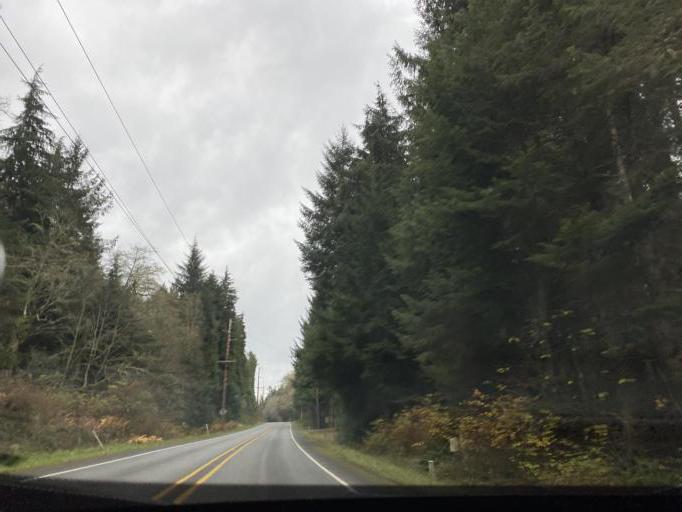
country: US
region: Washington
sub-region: Island County
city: Freeland
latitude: 48.0514
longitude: -122.5890
